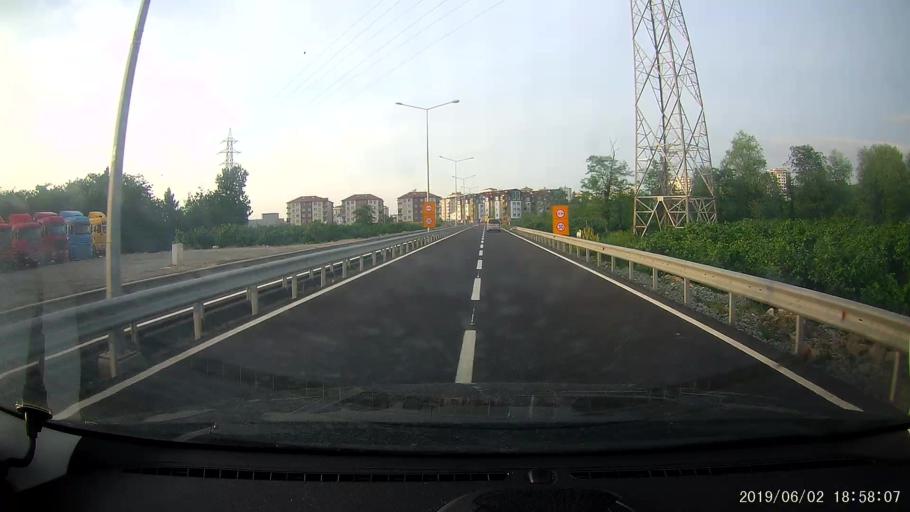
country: TR
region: Ordu
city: Ordu
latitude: 40.9578
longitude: 37.9068
